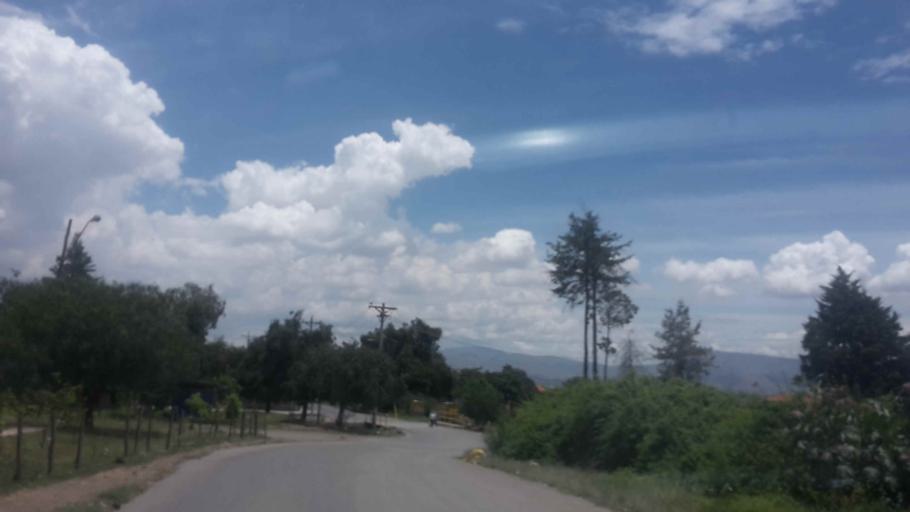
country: BO
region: Cochabamba
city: Cochabamba
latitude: -17.3442
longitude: -66.1782
